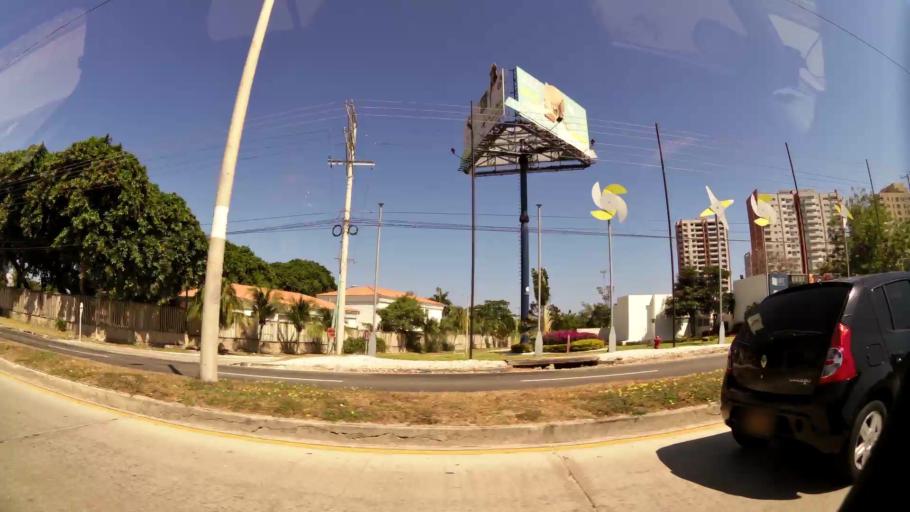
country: CO
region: Atlantico
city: Barranquilla
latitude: 11.0158
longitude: -74.8422
